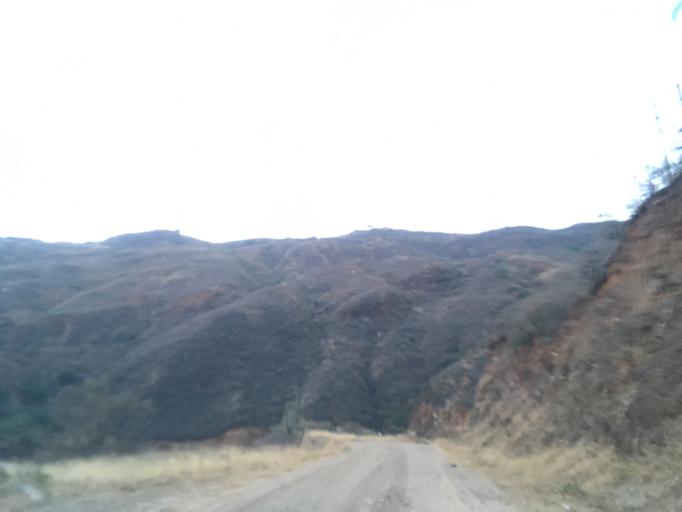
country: CO
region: Santander
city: Aratoca
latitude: 6.7927
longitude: -72.9959
